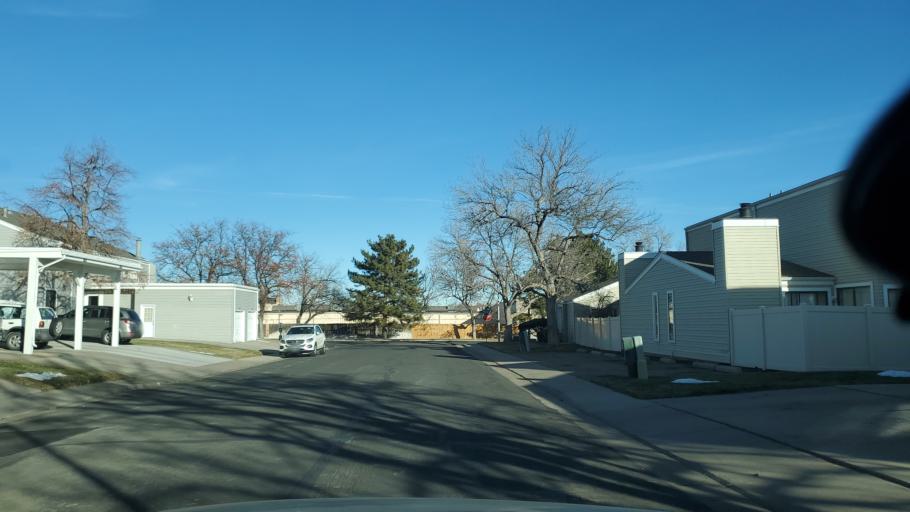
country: US
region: Colorado
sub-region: Adams County
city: Northglenn
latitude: 39.9110
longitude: -104.9422
